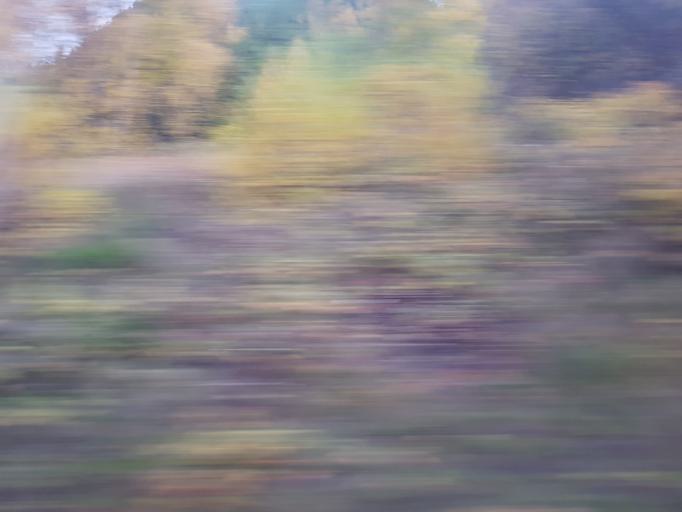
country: NO
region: Oppland
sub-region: Sel
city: Otta
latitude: 61.8441
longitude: 9.4116
